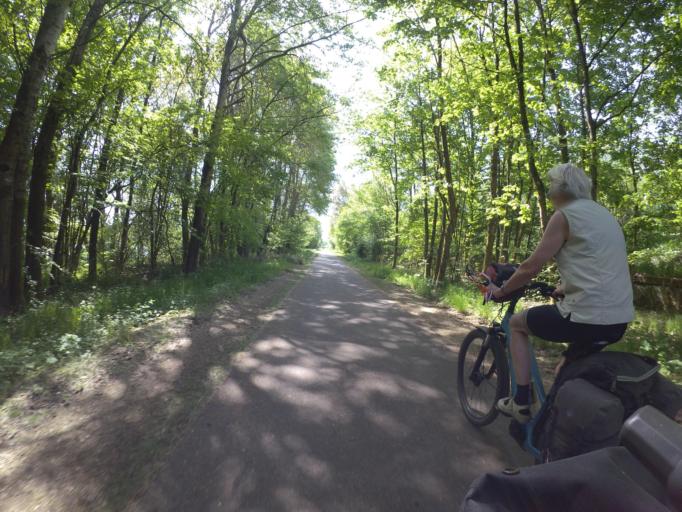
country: BE
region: Wallonia
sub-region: Province de Liege
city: Butgenbach
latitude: 50.4303
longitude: 6.2103
